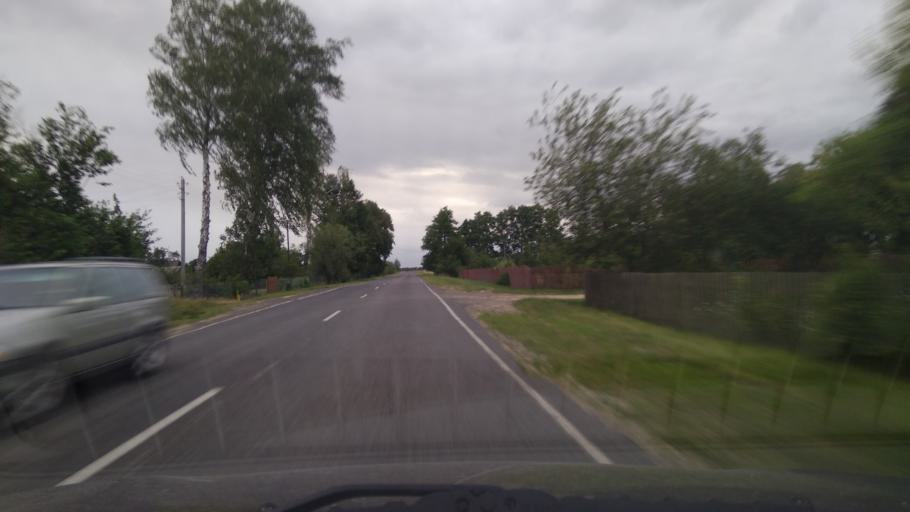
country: BY
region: Brest
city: Byaroza
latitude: 52.4253
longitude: 24.9810
